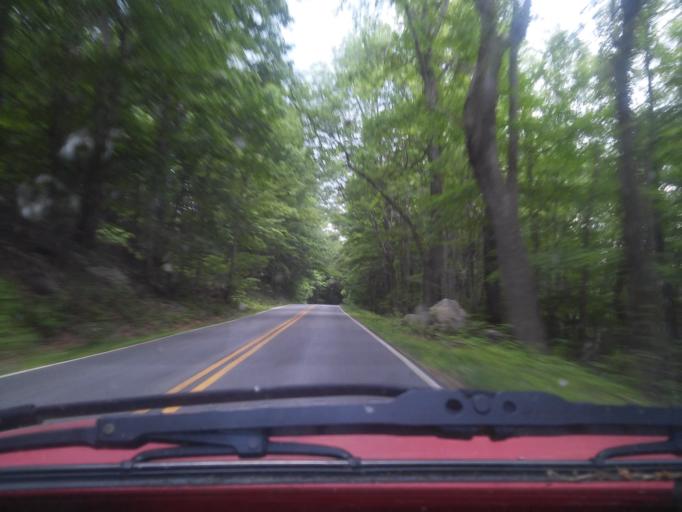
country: US
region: Virginia
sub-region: Giles County
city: Pembroke
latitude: 37.3282
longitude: -80.5465
